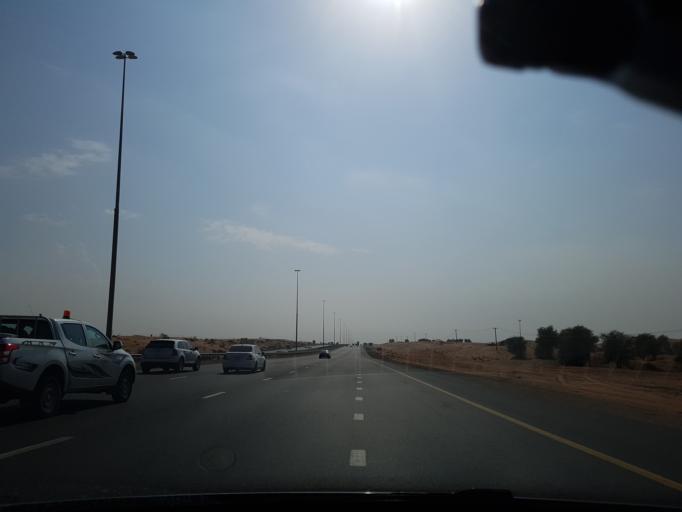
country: AE
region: Umm al Qaywayn
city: Umm al Qaywayn
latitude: 25.5244
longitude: 55.7192
